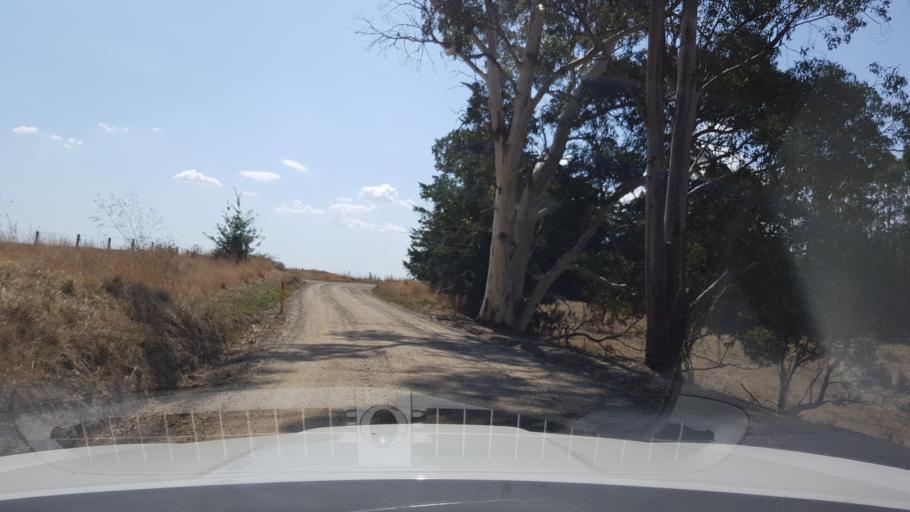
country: AU
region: Victoria
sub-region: Baw Baw
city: Warragul
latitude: -38.2980
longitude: 145.9129
